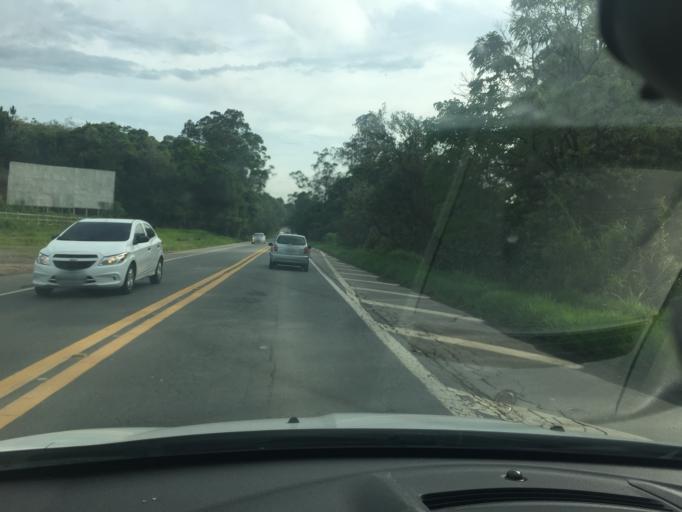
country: BR
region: Sao Paulo
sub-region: Campo Limpo Paulista
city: Campo Limpo Paulista
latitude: -23.1789
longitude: -46.7767
